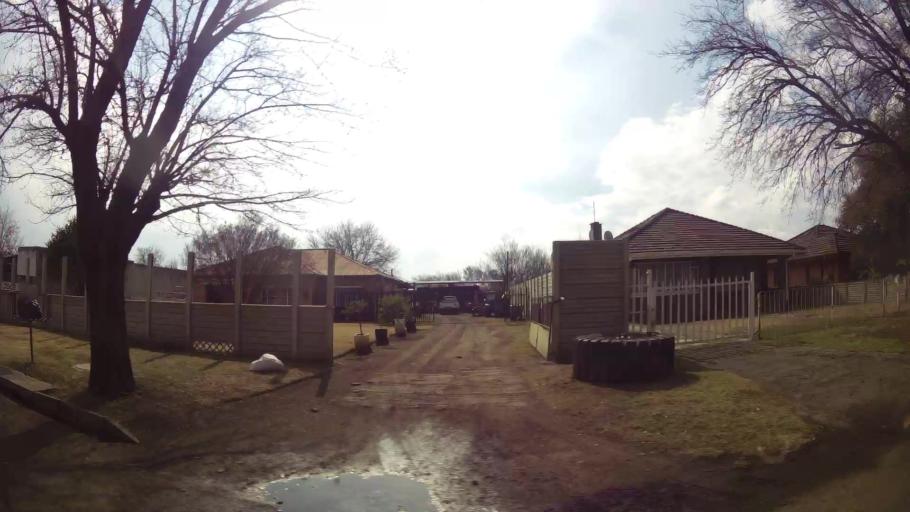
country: ZA
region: Gauteng
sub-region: Sedibeng District Municipality
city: Vereeniging
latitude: -26.6809
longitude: 27.9179
